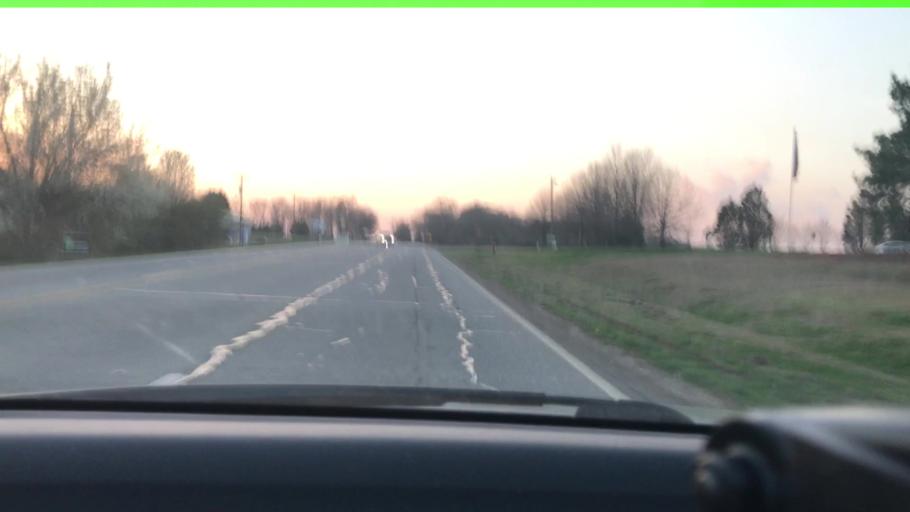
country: US
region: Georgia
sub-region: Oglethorpe County
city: Lexington
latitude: 33.8904
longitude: -83.1902
